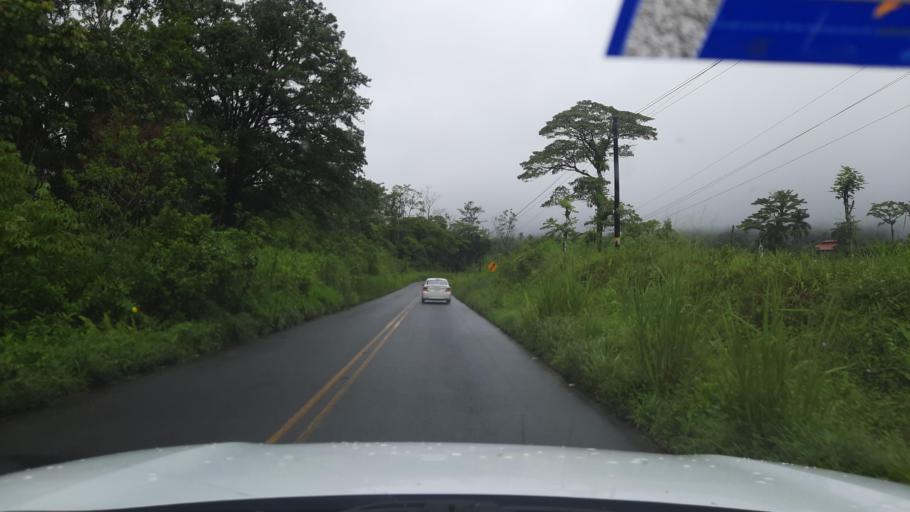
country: CR
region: Alajuela
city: Bijagua
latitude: 10.7733
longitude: -85.0295
